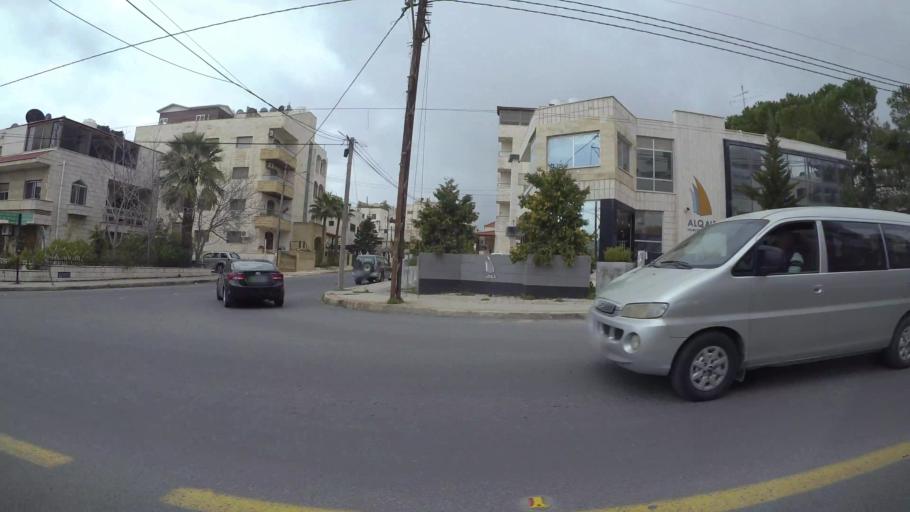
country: JO
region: Amman
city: Wadi as Sir
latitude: 31.9663
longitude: 35.8526
